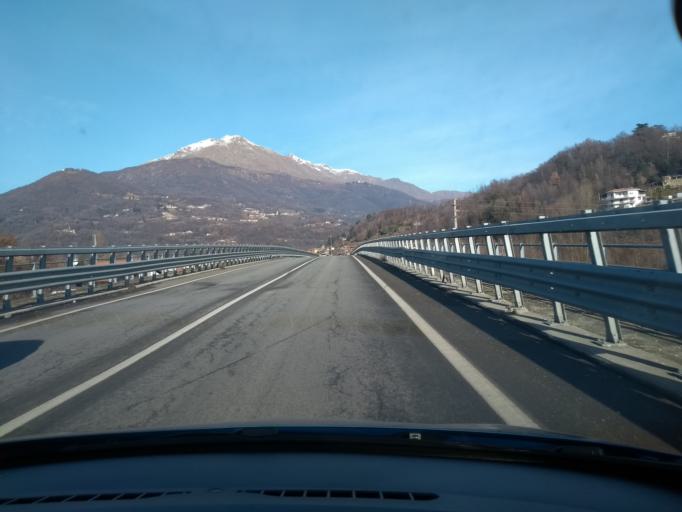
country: IT
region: Piedmont
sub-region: Provincia di Torino
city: Cuorgne
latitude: 45.3918
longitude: 7.6603
